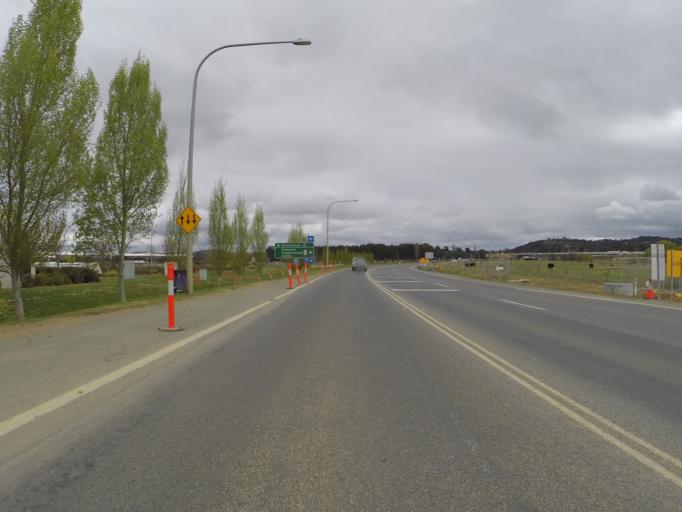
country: AU
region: Australian Capital Territory
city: Canberra
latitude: -35.2982
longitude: 149.1857
